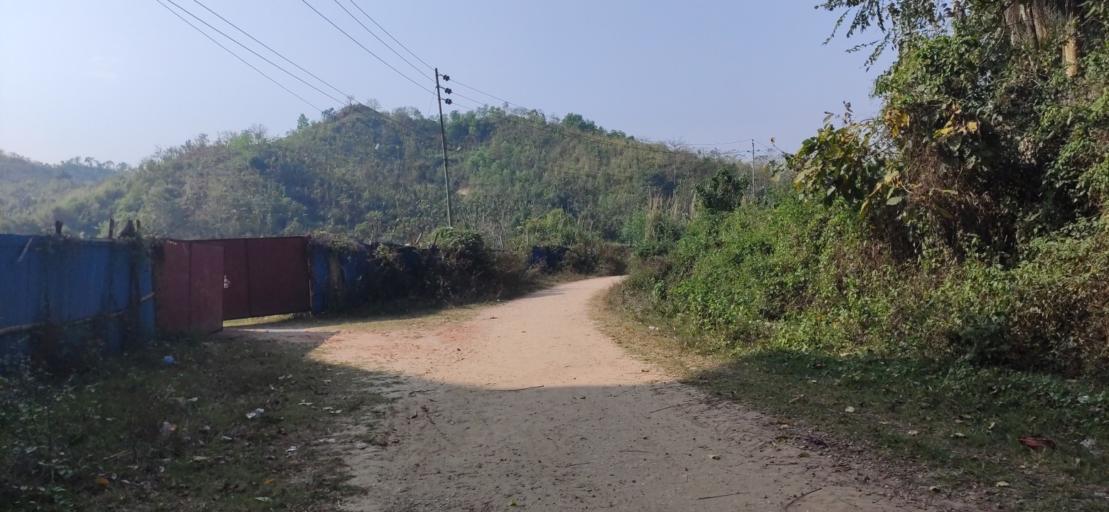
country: BD
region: Chittagong
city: Chittagong
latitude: 22.4739
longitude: 91.7847
